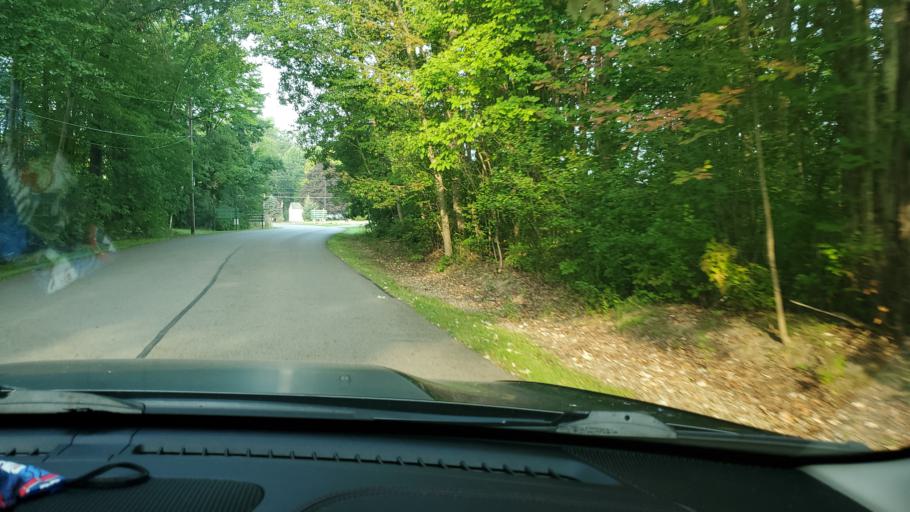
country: US
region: Ohio
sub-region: Mahoning County
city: Boardman
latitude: 41.0195
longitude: -80.6519
